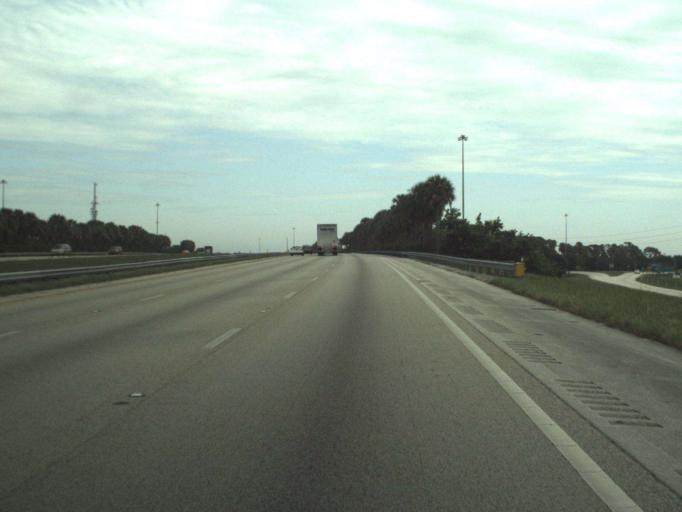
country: US
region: Florida
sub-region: Martin County
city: Palm City
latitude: 27.1056
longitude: -80.2588
